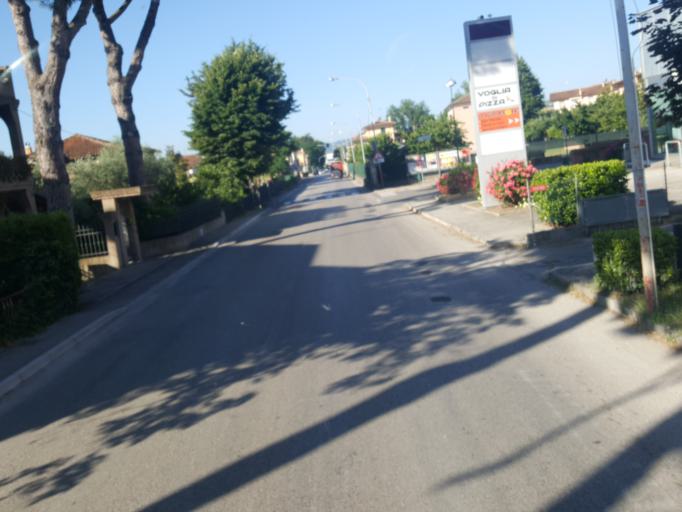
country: IT
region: The Marches
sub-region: Provincia di Pesaro e Urbino
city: Rio Salso-Case Bernardi
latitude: 43.8317
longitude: 12.6843
